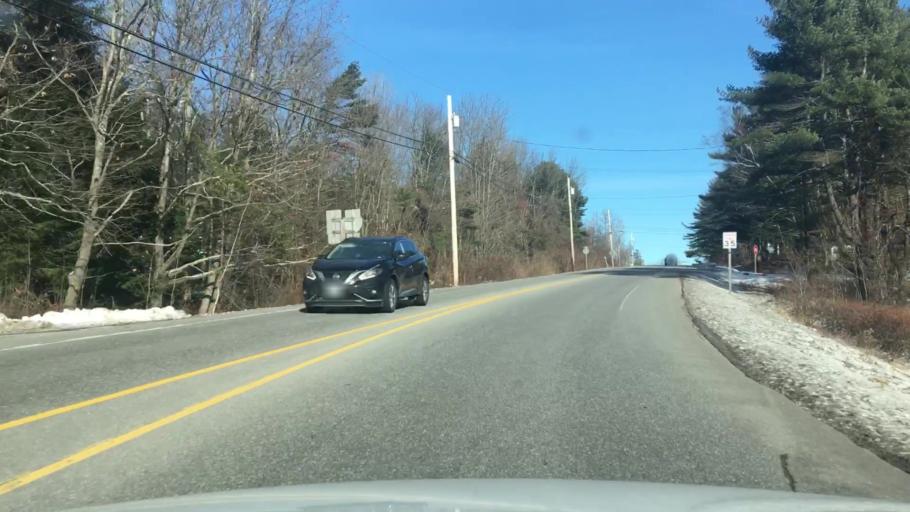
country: US
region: Maine
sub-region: Cumberland County
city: Freeport
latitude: 43.8664
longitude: -70.1095
